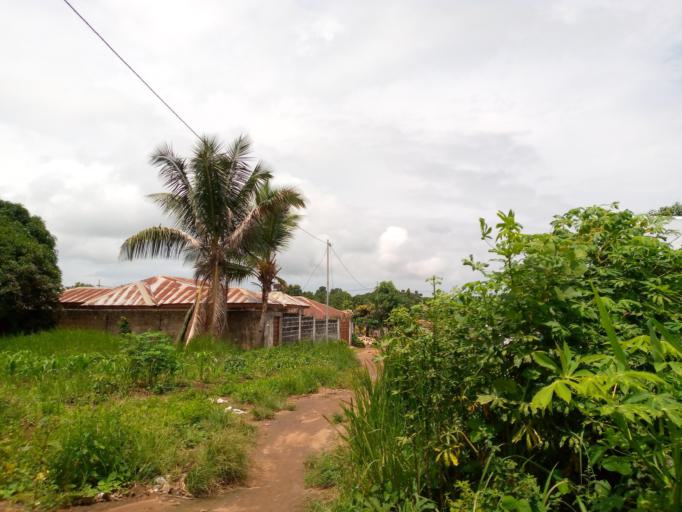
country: SL
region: Northern Province
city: Magburaka
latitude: 8.7258
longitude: -11.9359
